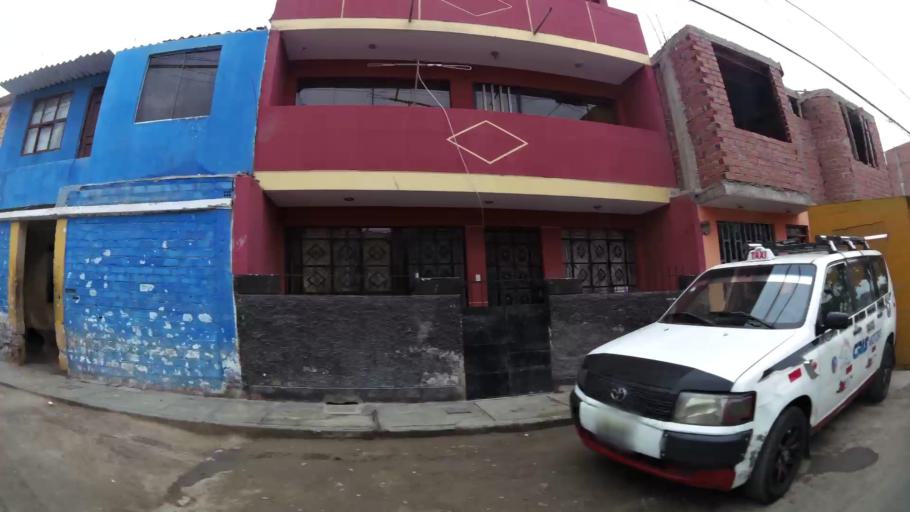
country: PE
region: Callao
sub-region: Callao
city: Callao
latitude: -12.0564
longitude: -77.1232
